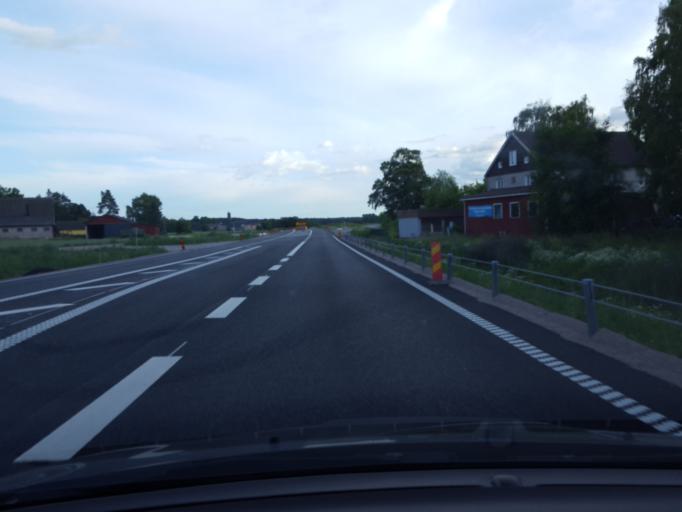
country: SE
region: Uppsala
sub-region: Osthammars Kommun
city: Gimo
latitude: 60.0932
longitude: 18.1224
